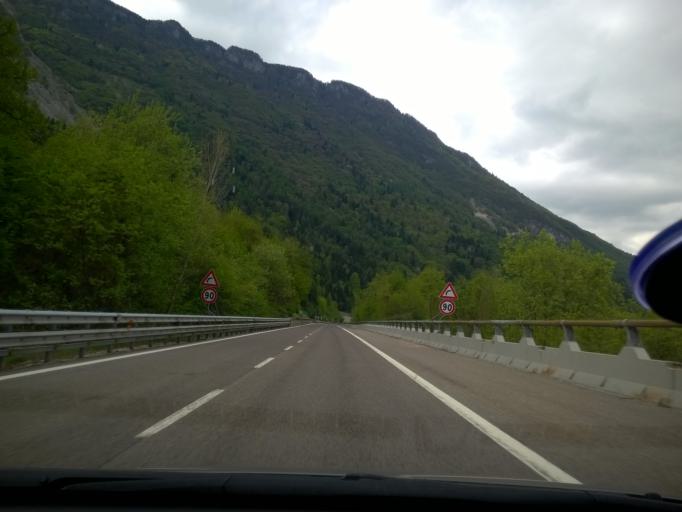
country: IT
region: Veneto
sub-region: Provincia di Belluno
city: Farra d'Alpago
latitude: 46.0920
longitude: 12.3278
